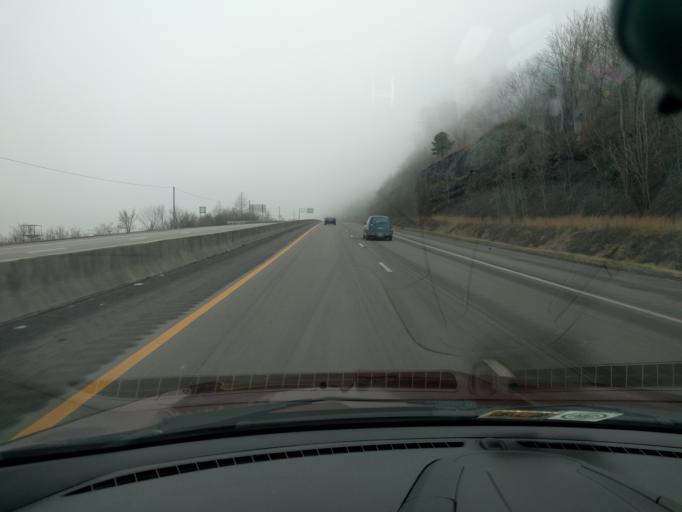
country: US
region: West Virginia
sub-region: Kanawha County
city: Chesapeake
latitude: 38.2050
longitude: -81.5032
